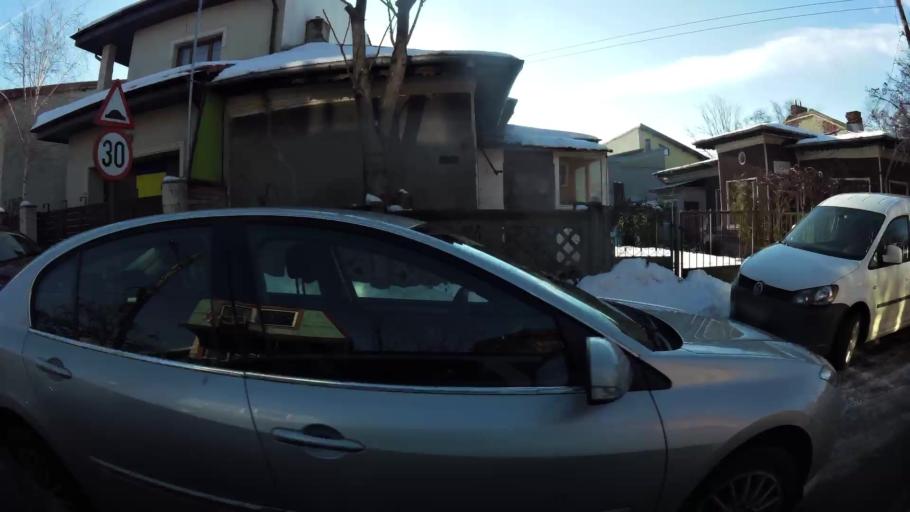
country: RO
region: Bucuresti
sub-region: Municipiul Bucuresti
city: Bucuresti
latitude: 44.3950
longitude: 26.0907
